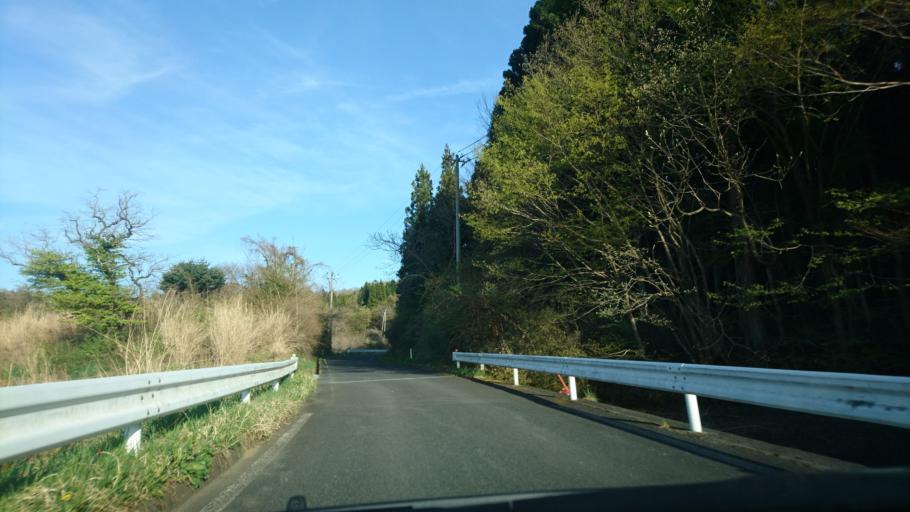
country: JP
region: Iwate
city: Ichinoseki
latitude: 38.8909
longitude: 141.2889
